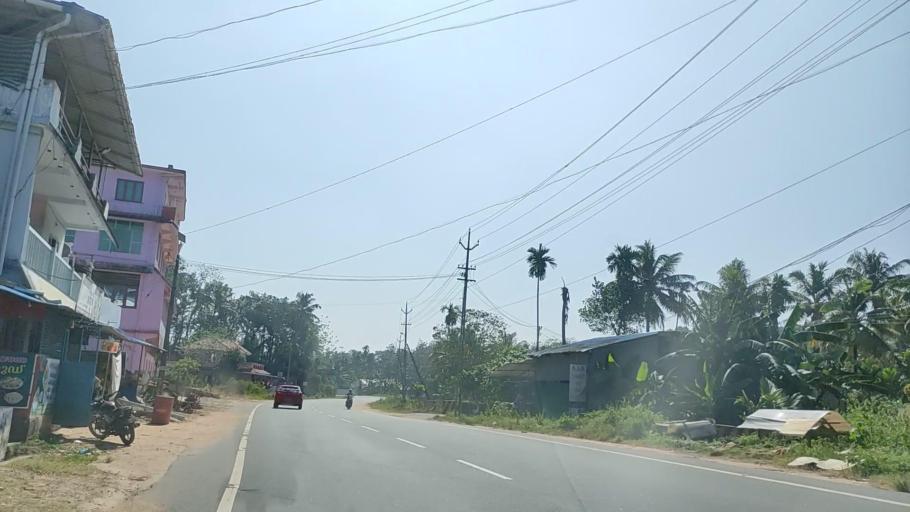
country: IN
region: Kerala
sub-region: Kollam
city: Punalur
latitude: 8.9110
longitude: 77.0481
